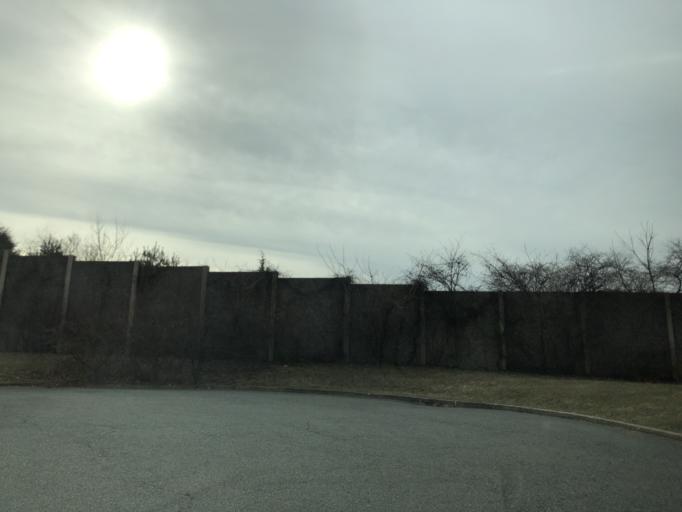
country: US
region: Pennsylvania
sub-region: Chester County
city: Exton
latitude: 40.0226
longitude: -75.6218
